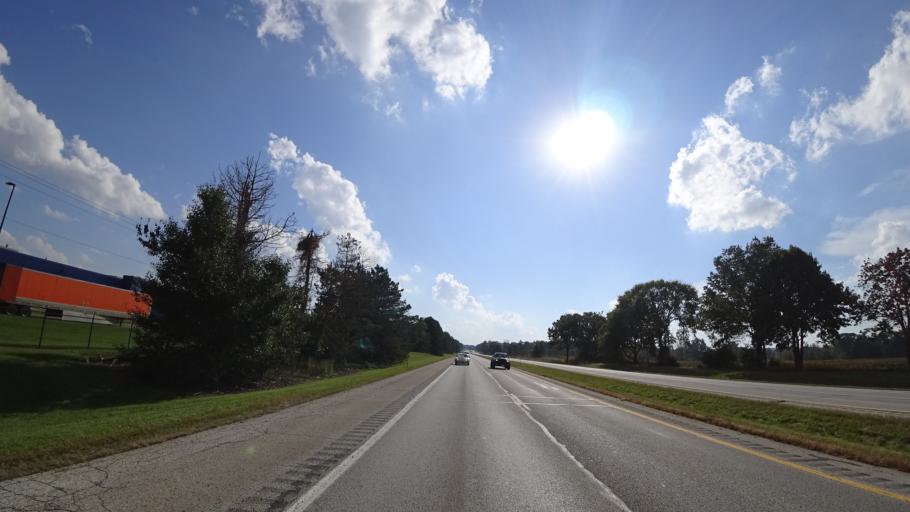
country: US
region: Michigan
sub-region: Saint Joseph County
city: Three Rivers
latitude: 41.9598
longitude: -85.6429
